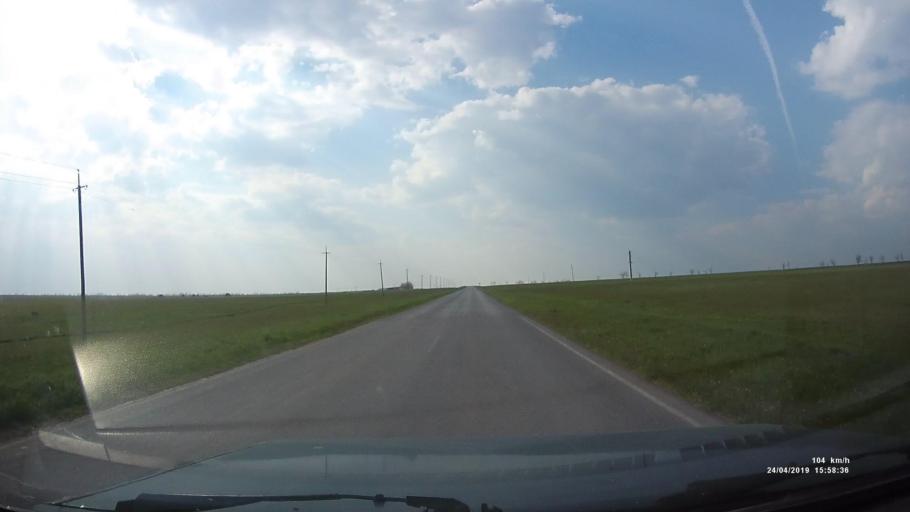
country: RU
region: Kalmykiya
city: Yashalta
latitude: 46.6158
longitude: 42.4871
